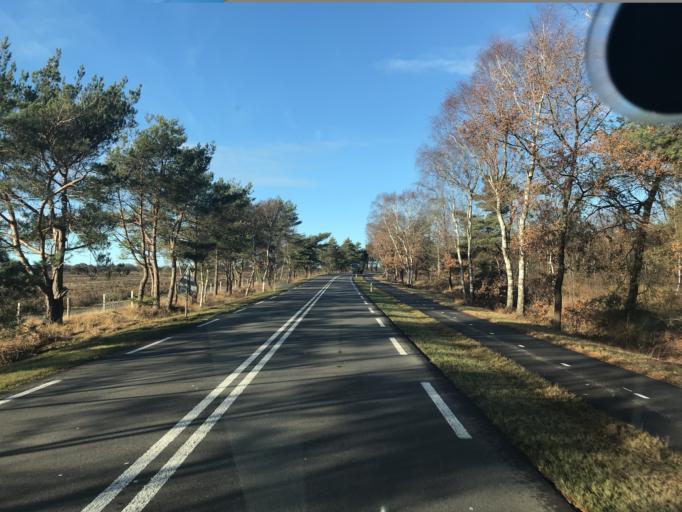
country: NL
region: Gelderland
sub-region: Gemeente Barneveld
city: Garderen
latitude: 52.2854
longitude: 5.6883
